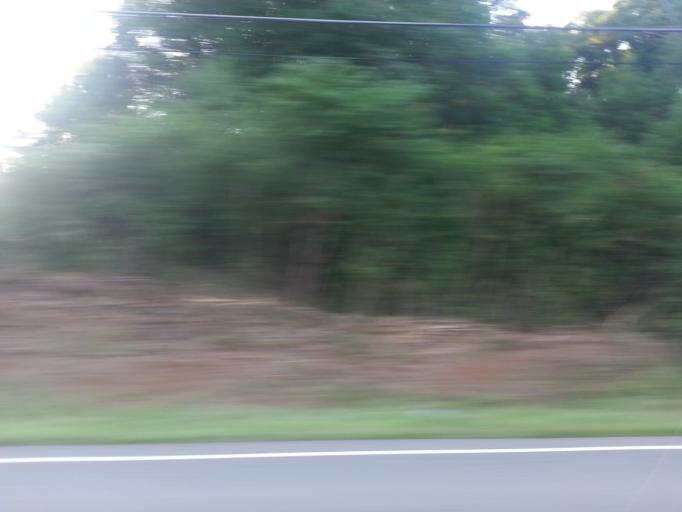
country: US
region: Tennessee
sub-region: Loudon County
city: Lenoir City
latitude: 35.8394
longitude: -84.2346
